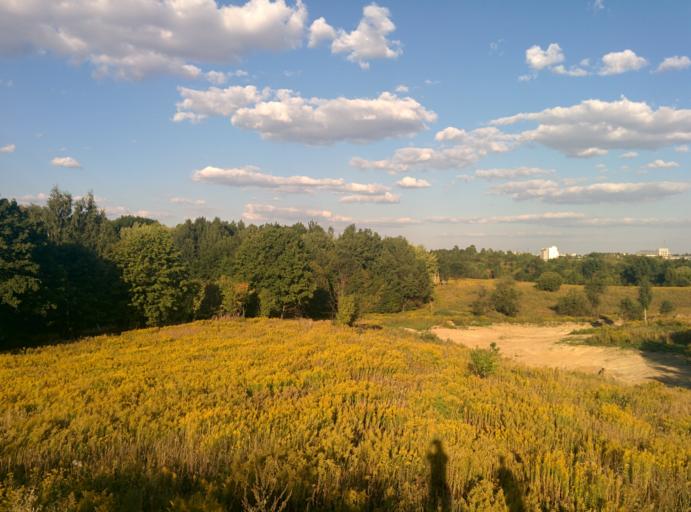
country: BY
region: Minsk
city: Novoye Medvezhino
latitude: 53.8860
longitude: 27.4647
